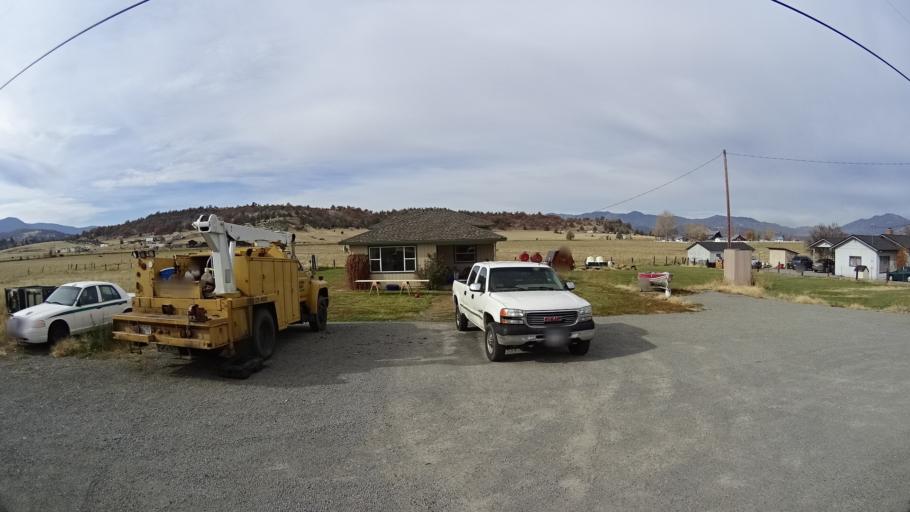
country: US
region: California
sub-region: Siskiyou County
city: Montague
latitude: 41.7037
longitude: -122.5630
